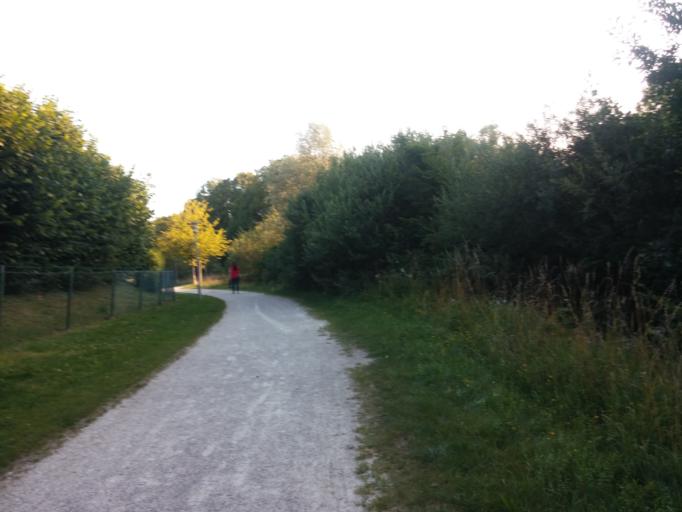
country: DE
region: Bavaria
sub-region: Upper Bavaria
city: Markt Schwaben
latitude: 48.1914
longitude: 11.8612
